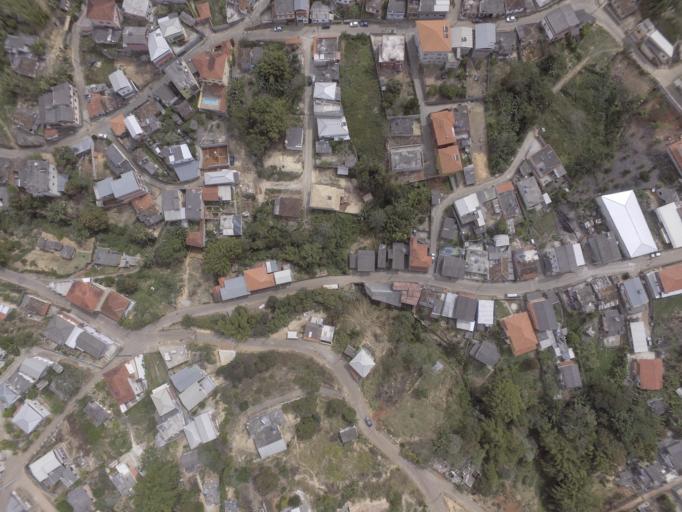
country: BR
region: Minas Gerais
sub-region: Tiradentes
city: Tiradentes
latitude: -21.0541
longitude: -44.0752
